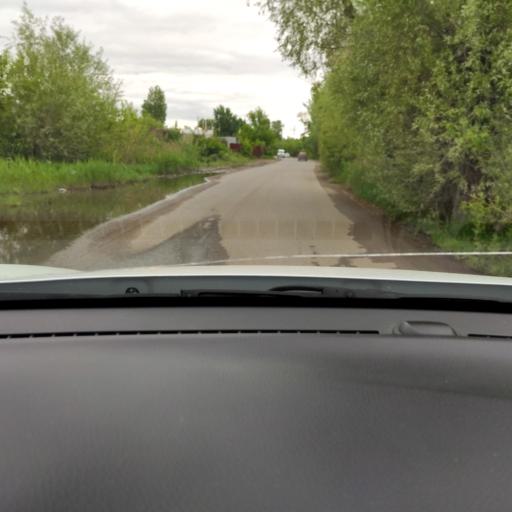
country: RU
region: Tatarstan
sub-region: Gorod Kazan'
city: Kazan
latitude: 55.7784
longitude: 49.0970
